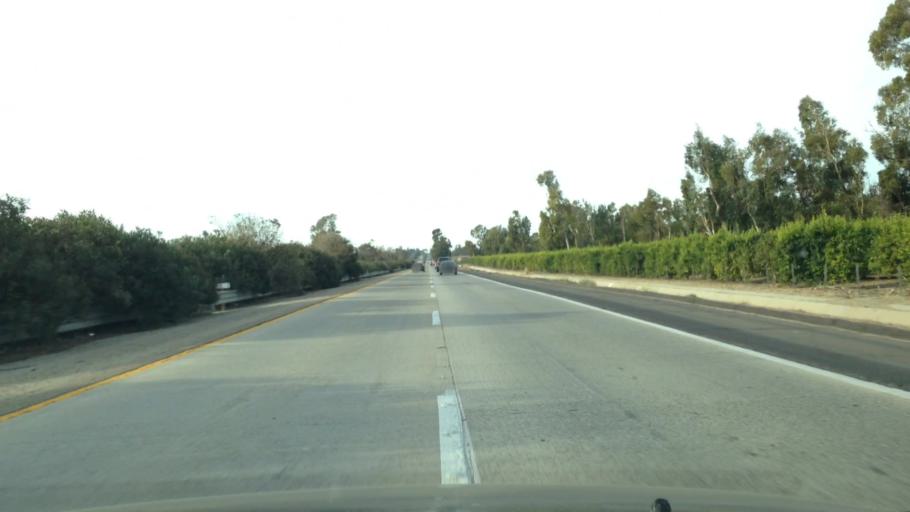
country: US
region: California
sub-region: Ventura County
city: Saticoy
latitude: 34.2997
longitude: -119.1397
